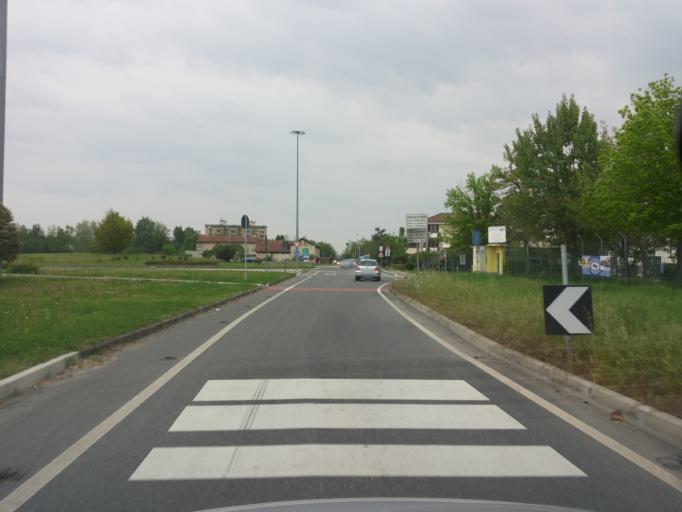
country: IT
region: Piedmont
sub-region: Provincia di Alessandria
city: Casale Monferrato
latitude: 45.1147
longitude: 8.4515
